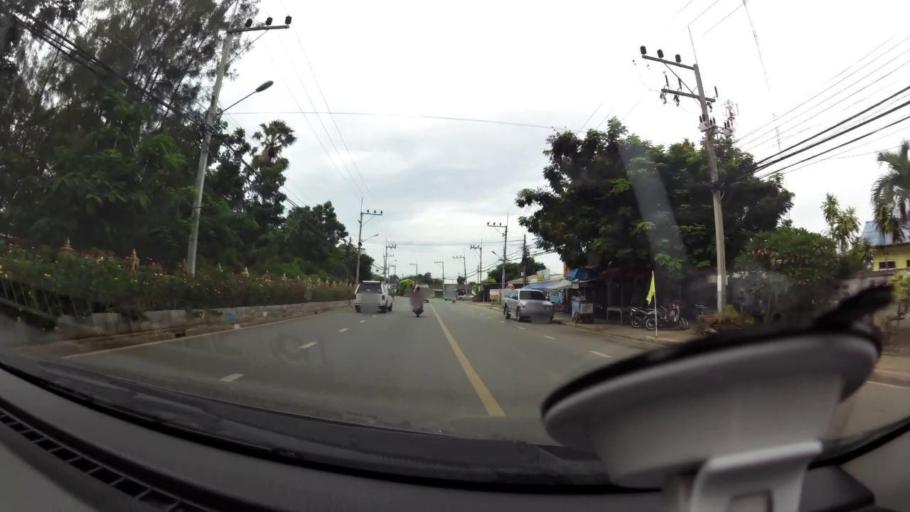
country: TH
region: Prachuap Khiri Khan
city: Pran Buri
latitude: 12.3949
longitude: 99.9891
